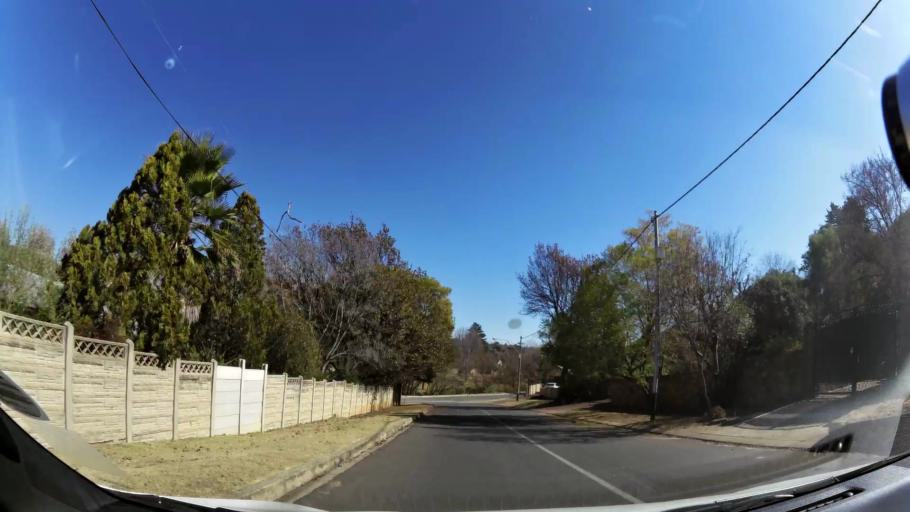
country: ZA
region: Gauteng
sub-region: City of Johannesburg Metropolitan Municipality
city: Johannesburg
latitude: -26.2712
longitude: 28.0022
